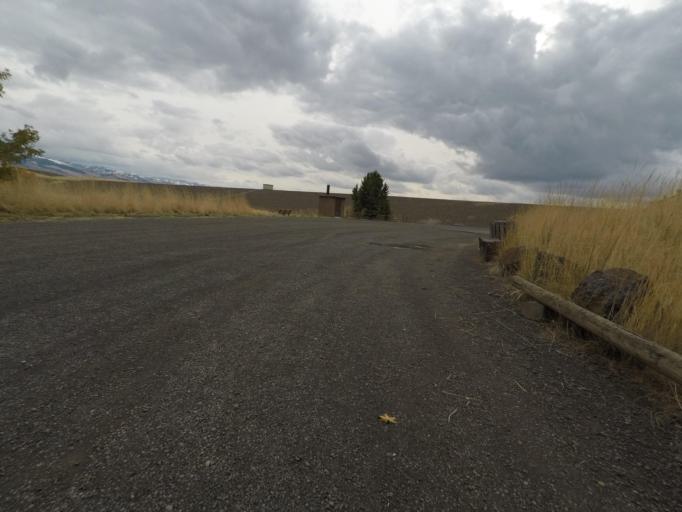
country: US
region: Washington
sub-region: Walla Walla County
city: Walla Walla East
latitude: 46.0662
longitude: -118.2643
